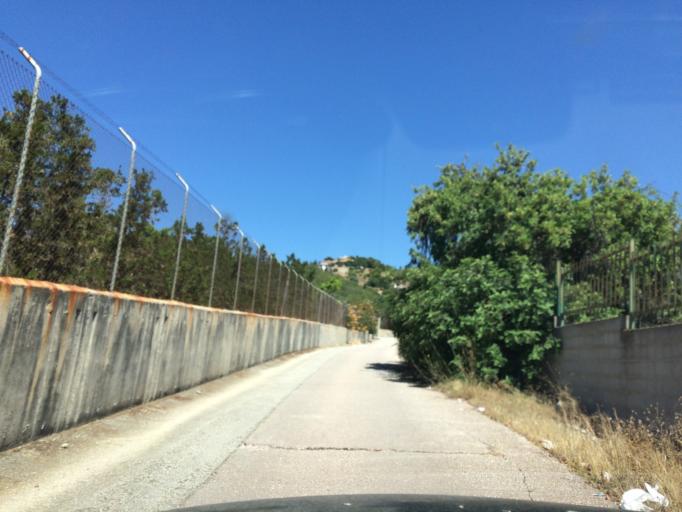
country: ES
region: Andalusia
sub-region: Provincia de Malaga
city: Malaga
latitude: 36.7366
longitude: -4.4662
